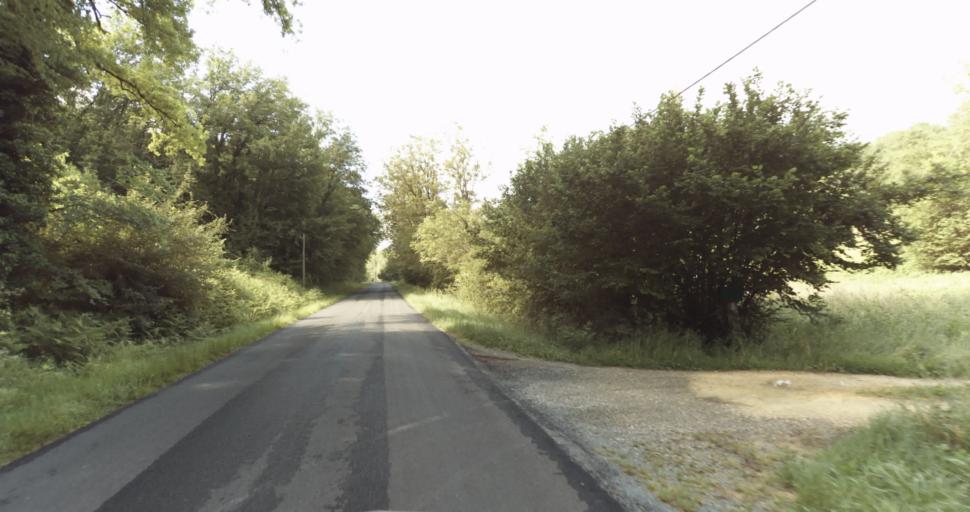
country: FR
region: Aquitaine
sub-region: Departement de la Dordogne
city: Lalinde
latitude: 44.8593
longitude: 0.7748
